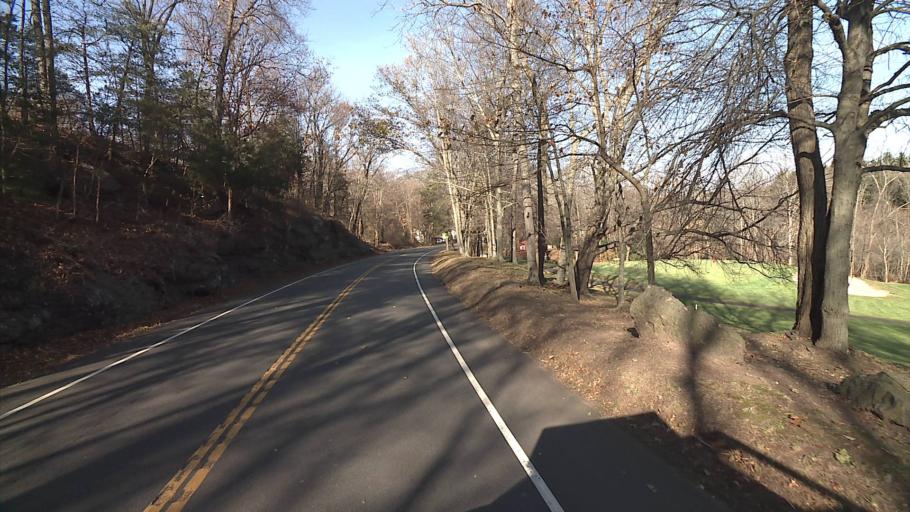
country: US
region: Connecticut
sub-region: Middlesex County
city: Portland
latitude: 41.5869
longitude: -72.6119
